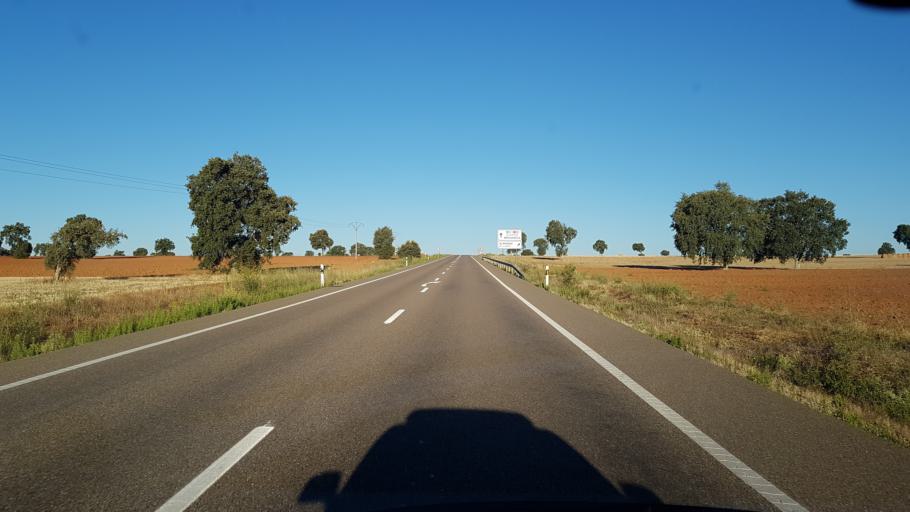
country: ES
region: Castille and Leon
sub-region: Provincia de Zamora
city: Palacios del Pan
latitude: 41.5432
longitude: -5.9080
